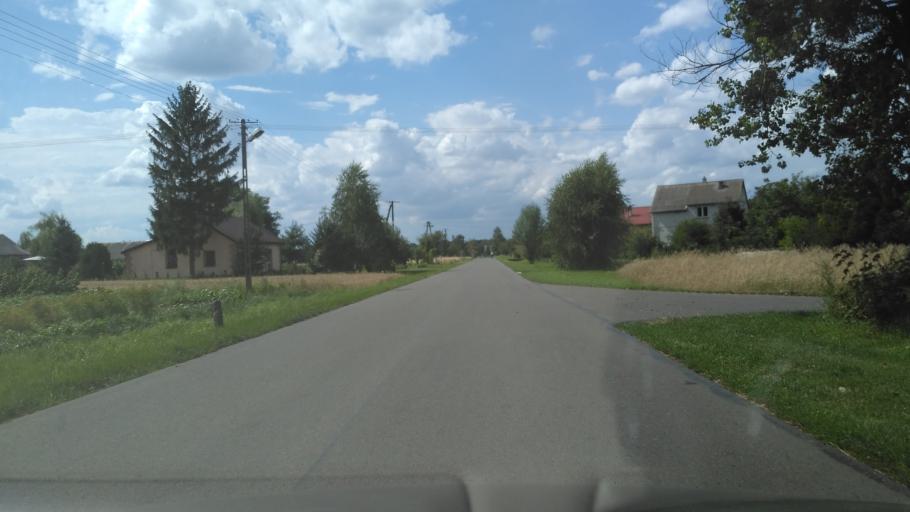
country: PL
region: Lublin Voivodeship
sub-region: Powiat leczynski
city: Milejow
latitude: 51.1846
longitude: 22.9513
